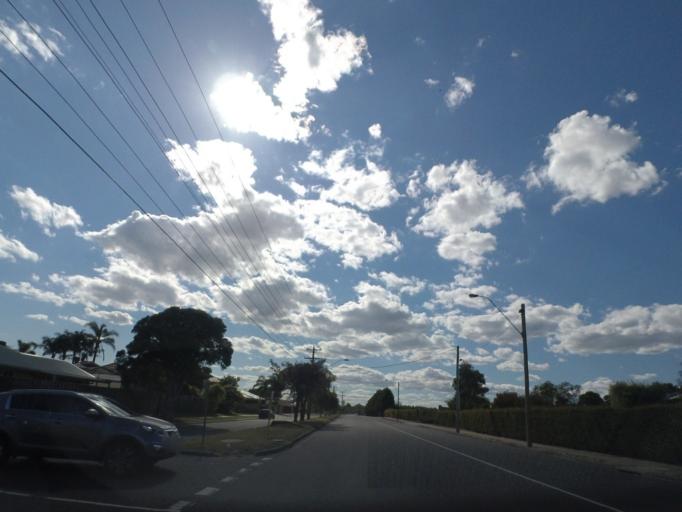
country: AU
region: Victoria
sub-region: Kingston
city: Dingley Village
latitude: -37.9783
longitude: 145.1252
